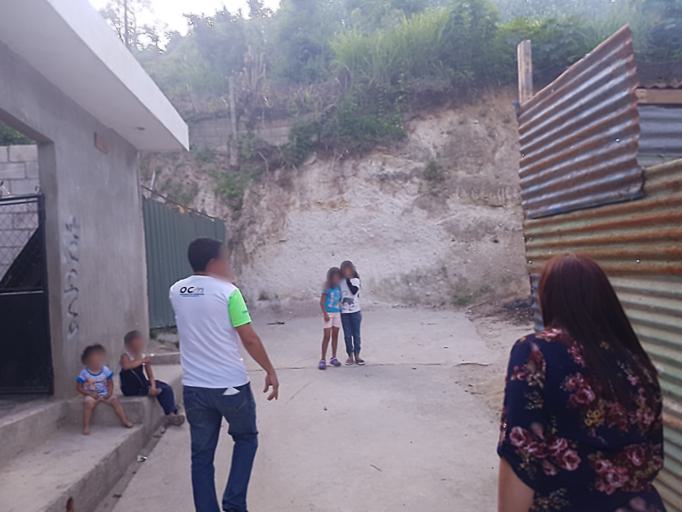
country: GT
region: Guatemala
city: Petapa
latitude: 14.5027
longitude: -90.5544
